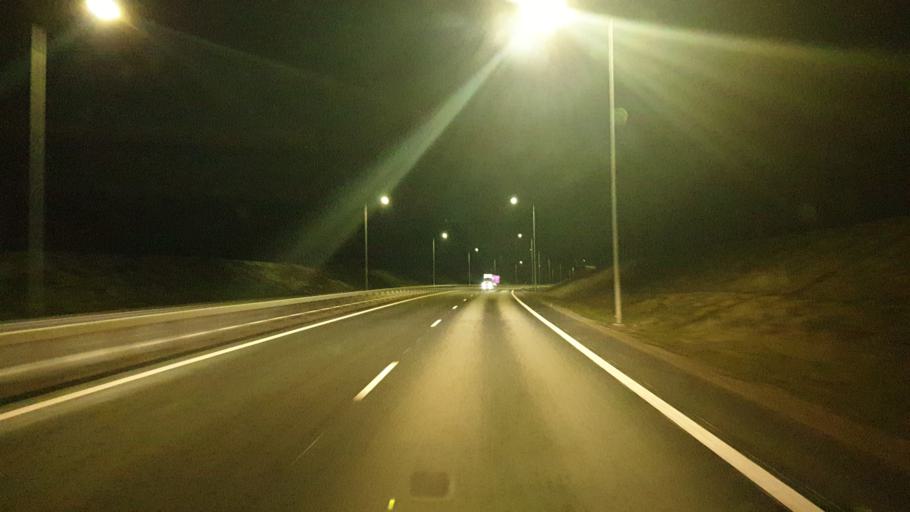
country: FI
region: Central Finland
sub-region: AEaenekoski
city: AEaenekoski
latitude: 62.5975
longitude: 25.6899
